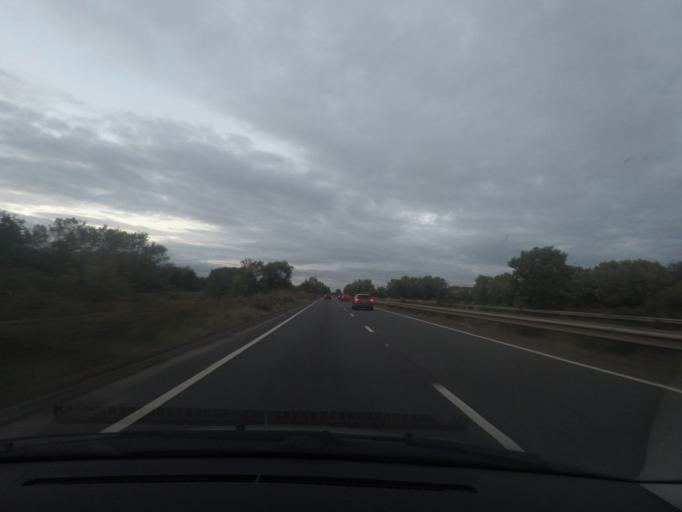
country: GB
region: England
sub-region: Northamptonshire
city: Higham Ferrers
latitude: 52.3095
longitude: -0.6070
